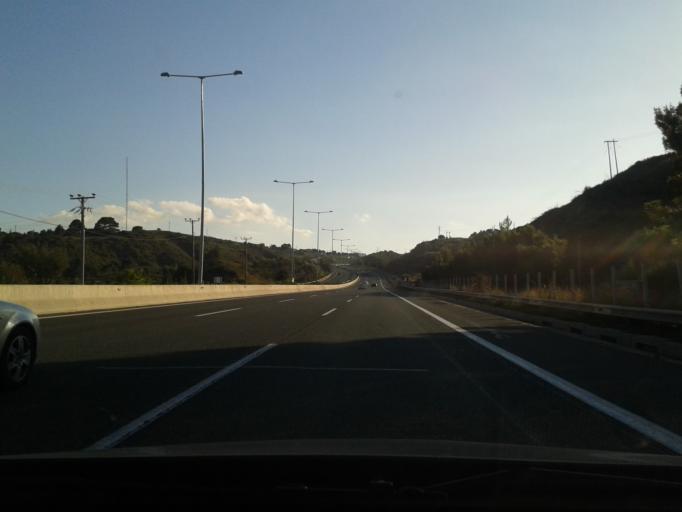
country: GR
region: Attica
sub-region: Nomarchia Anatolikis Attikis
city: Agios Stefanos
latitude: 38.1634
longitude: 23.8560
